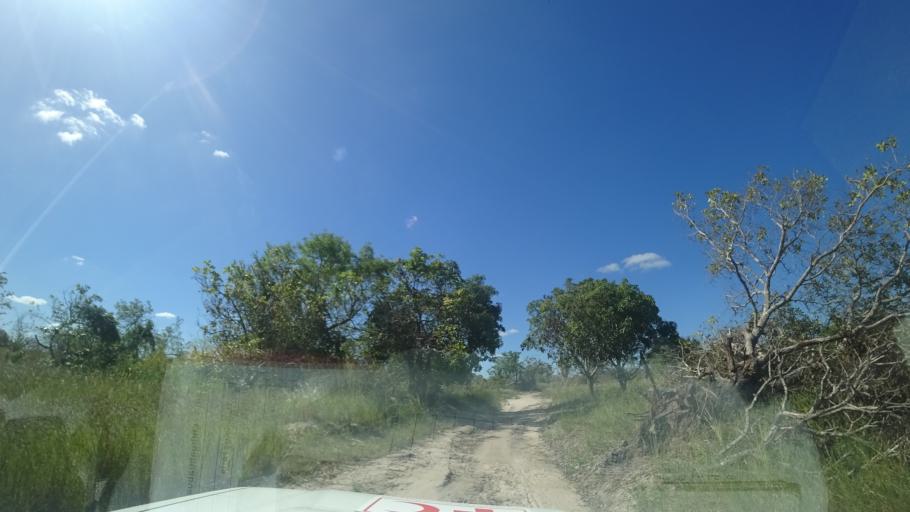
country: MZ
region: Sofala
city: Dondo
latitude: -19.4837
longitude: 34.6189
